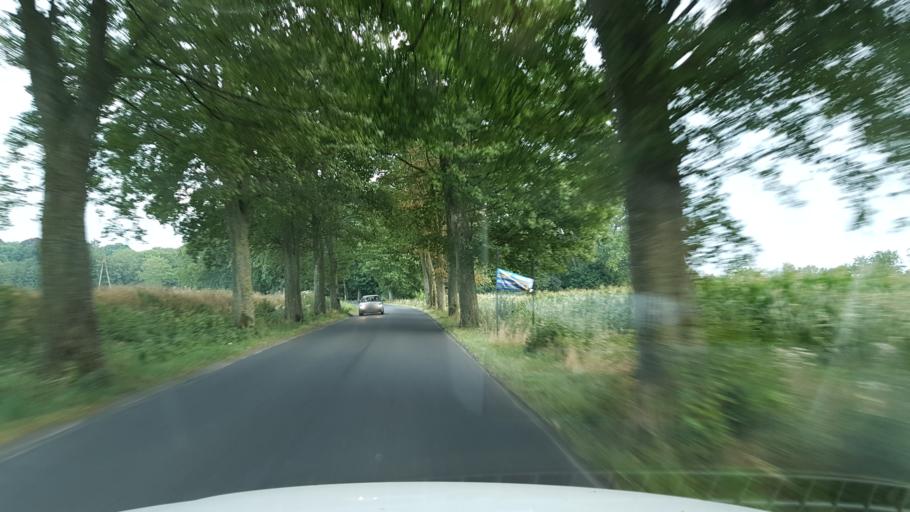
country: PL
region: West Pomeranian Voivodeship
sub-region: Powiat koszalinski
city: Mielno
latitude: 54.2307
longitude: 16.0199
